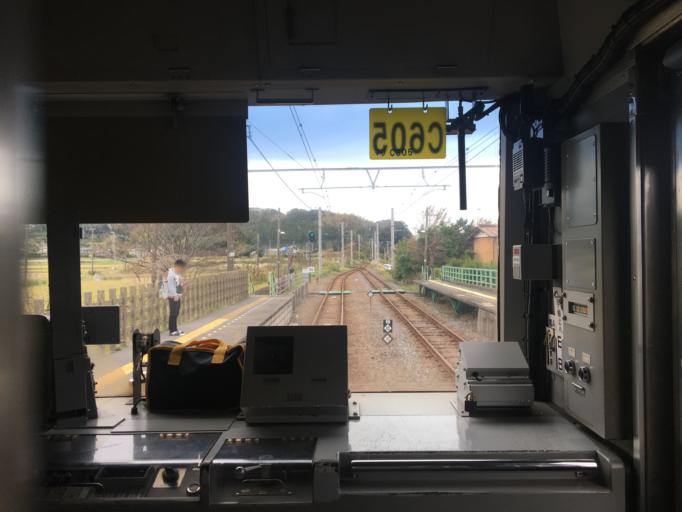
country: JP
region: Chiba
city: Tateyama
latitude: 34.9977
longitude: 139.9108
